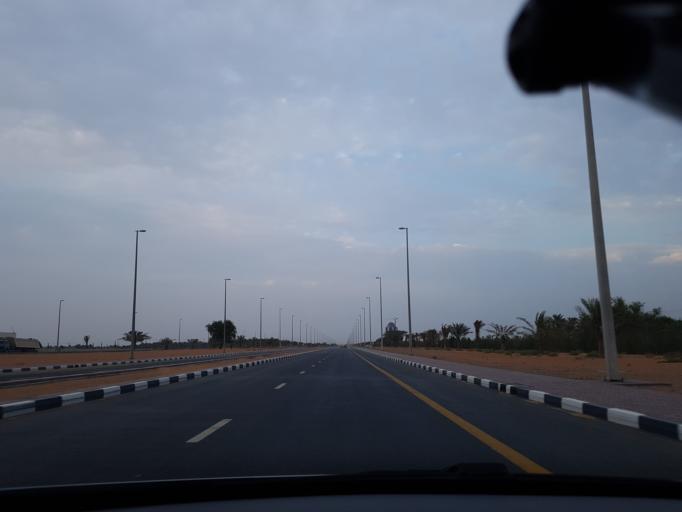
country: AE
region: Ash Shariqah
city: Adh Dhayd
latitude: 25.2731
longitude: 55.9123
